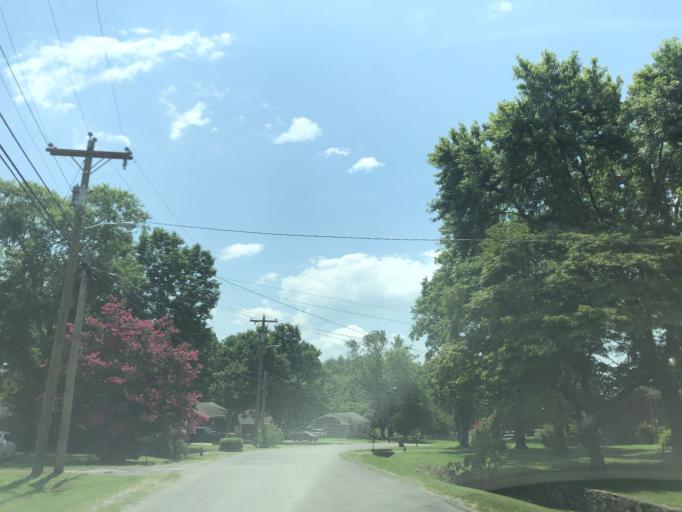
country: US
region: Tennessee
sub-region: Davidson County
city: Lakewood
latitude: 36.1534
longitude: -86.6589
